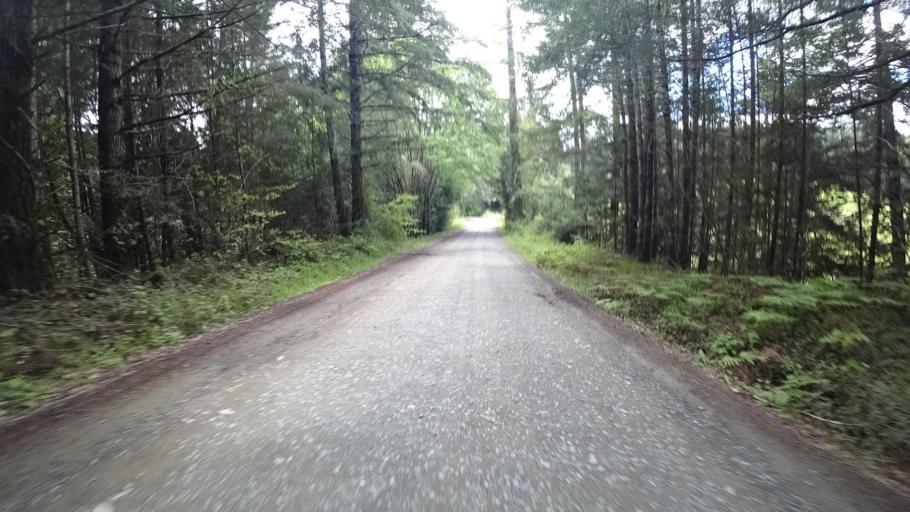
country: US
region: California
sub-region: Humboldt County
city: Blue Lake
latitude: 40.7869
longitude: -123.8807
